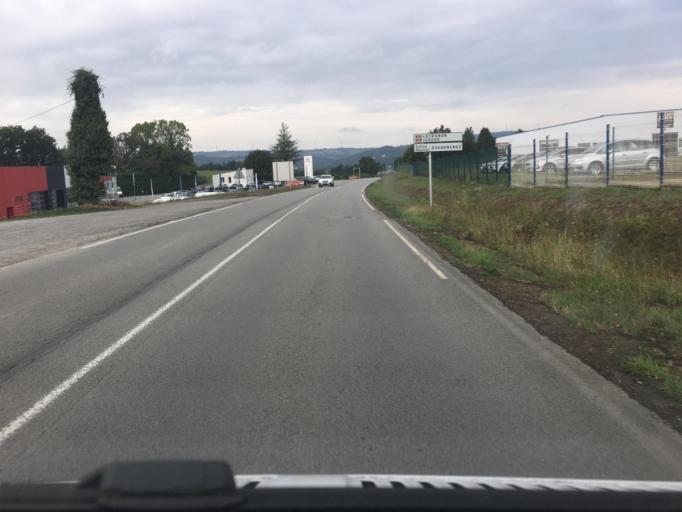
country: FR
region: Brittany
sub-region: Departement du Finistere
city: Chateaulin
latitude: 48.2075
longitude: -4.0688
